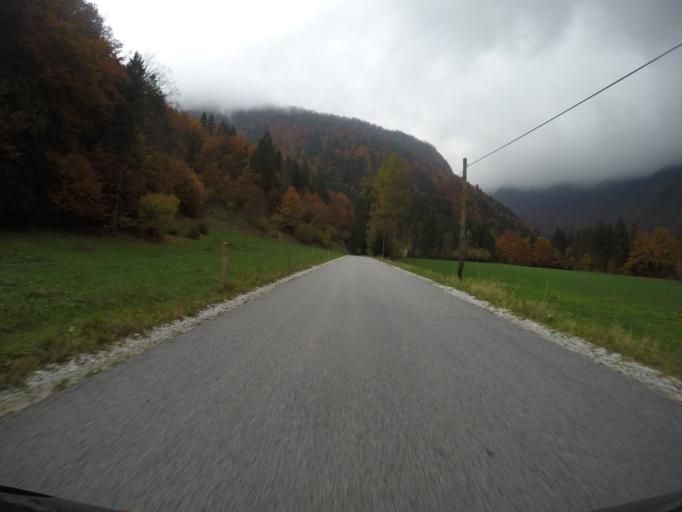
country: SI
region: Jesenice
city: Hrusica
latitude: 46.4047
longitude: 14.0006
